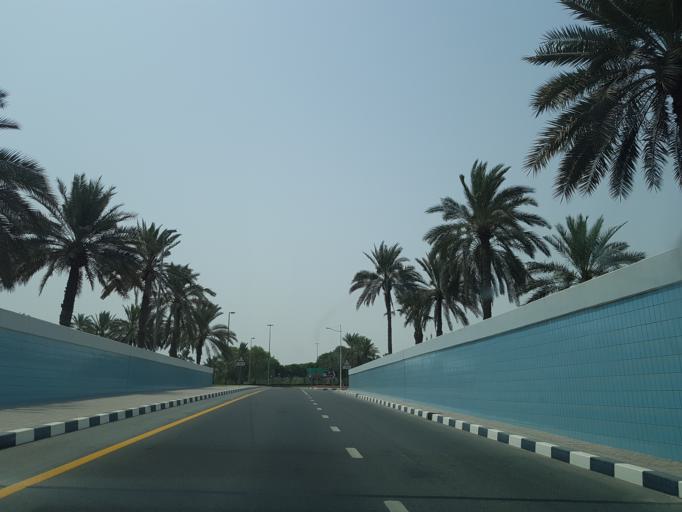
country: AE
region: Ash Shariqah
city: Sharjah
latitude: 25.2295
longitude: 55.2992
